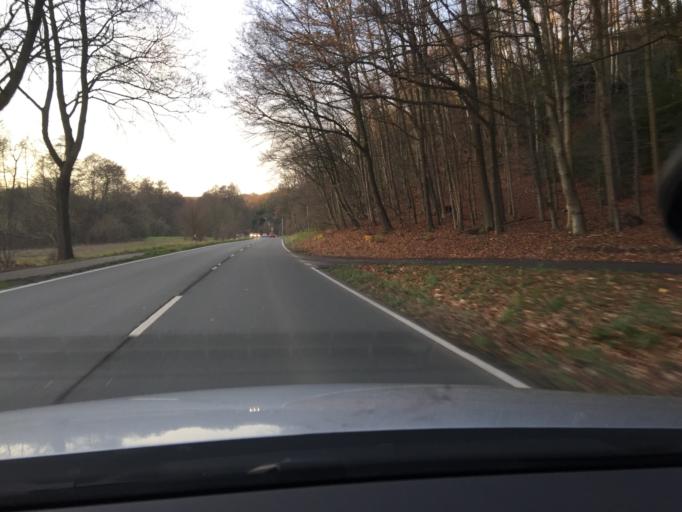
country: DE
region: North Rhine-Westphalia
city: Hattingen
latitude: 51.3673
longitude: 7.1900
